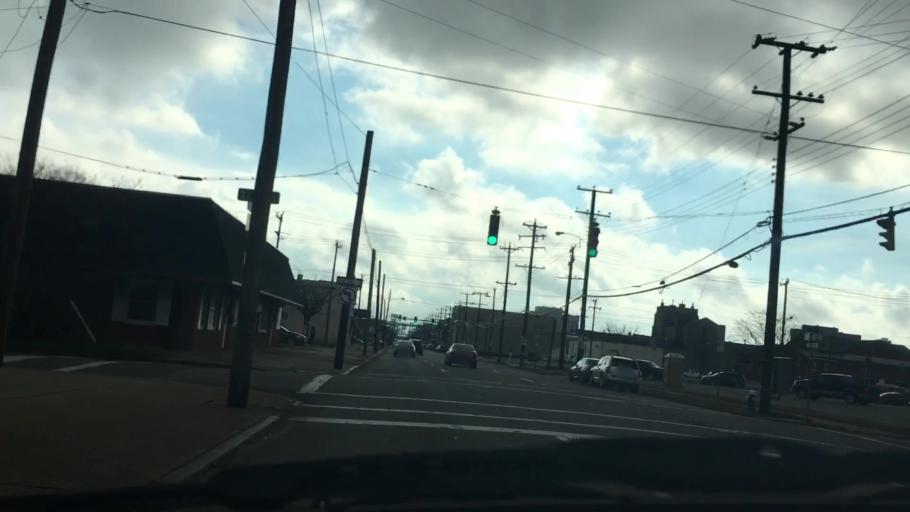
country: US
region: Virginia
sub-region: City of Newport News
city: Newport News
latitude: 36.9863
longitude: -76.4333
